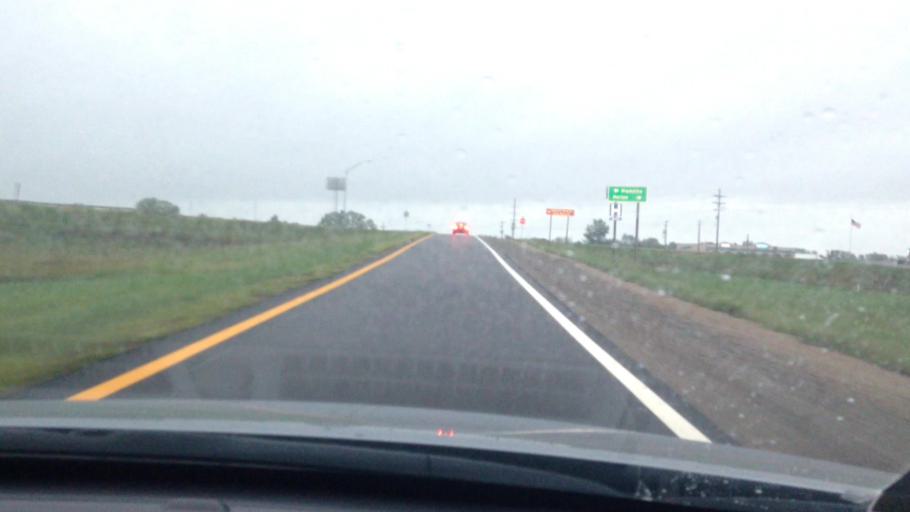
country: US
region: Kansas
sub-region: Brown County
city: Hiawatha
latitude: 39.8403
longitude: -95.5289
